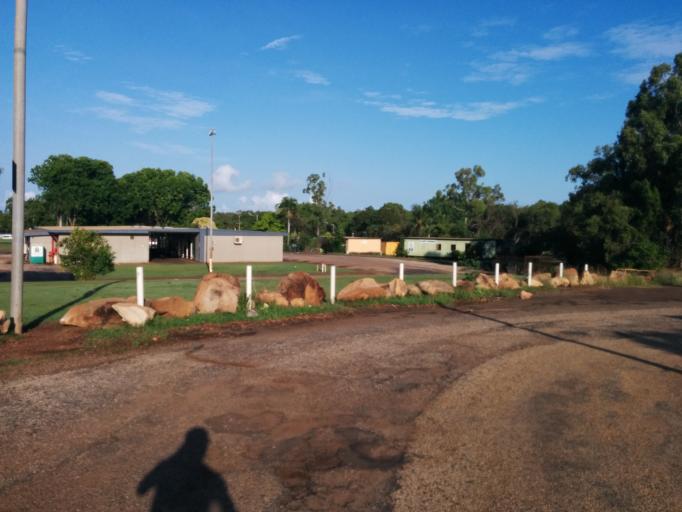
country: AU
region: Northern Territory
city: Alyangula
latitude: -13.8489
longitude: 136.4186
